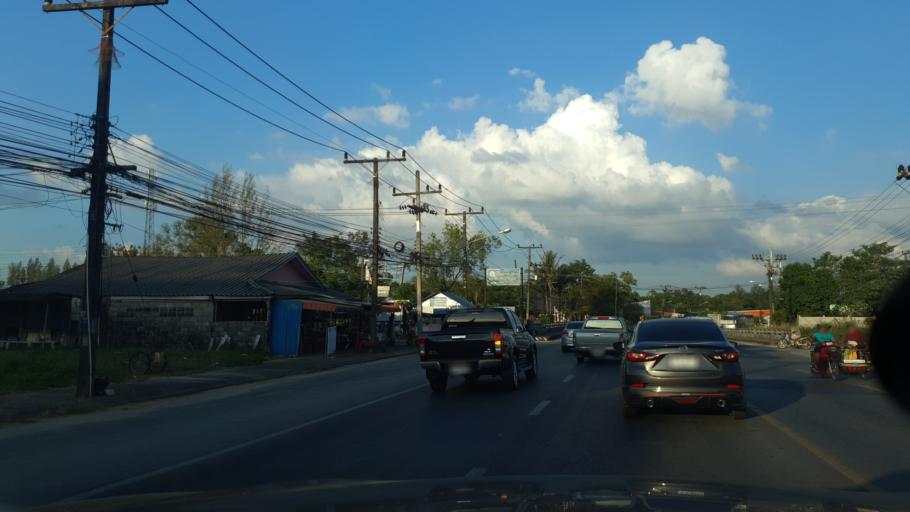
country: TH
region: Phangnga
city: Takua Pa
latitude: 8.8445
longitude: 98.2894
